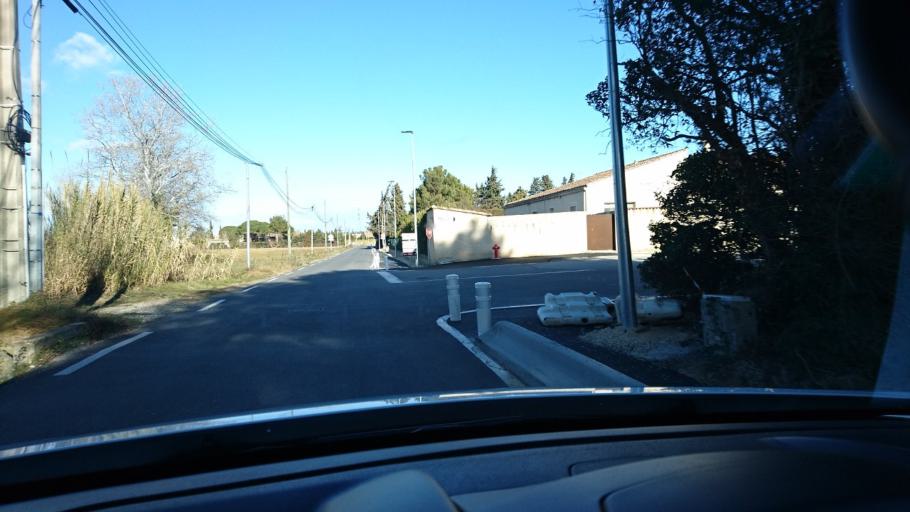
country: FR
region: Provence-Alpes-Cote d'Azur
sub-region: Departement du Vaucluse
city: Morieres-les-Avignon
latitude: 43.9288
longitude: 4.9060
